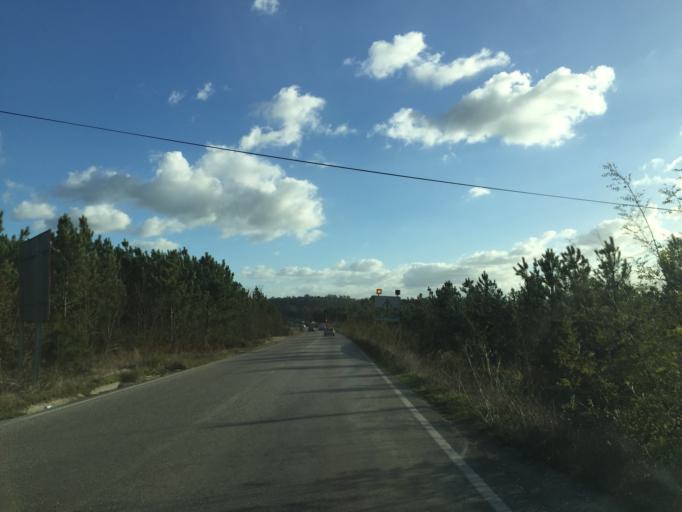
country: PT
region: Leiria
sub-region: Leiria
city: Monte Redondo
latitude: 39.8722
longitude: -8.8390
